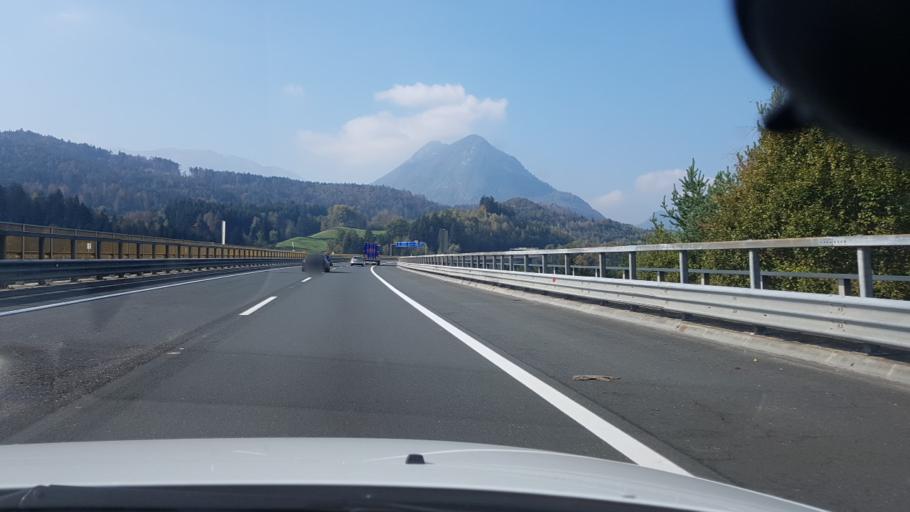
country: AT
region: Carinthia
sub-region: Villach Stadt
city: Villach
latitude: 46.6418
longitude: 13.8095
